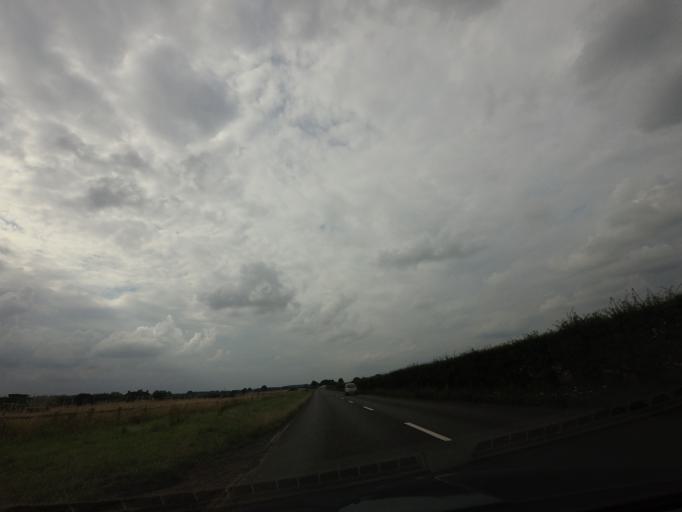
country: GB
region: England
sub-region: Shropshire
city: Tong
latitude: 52.6892
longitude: -2.3145
